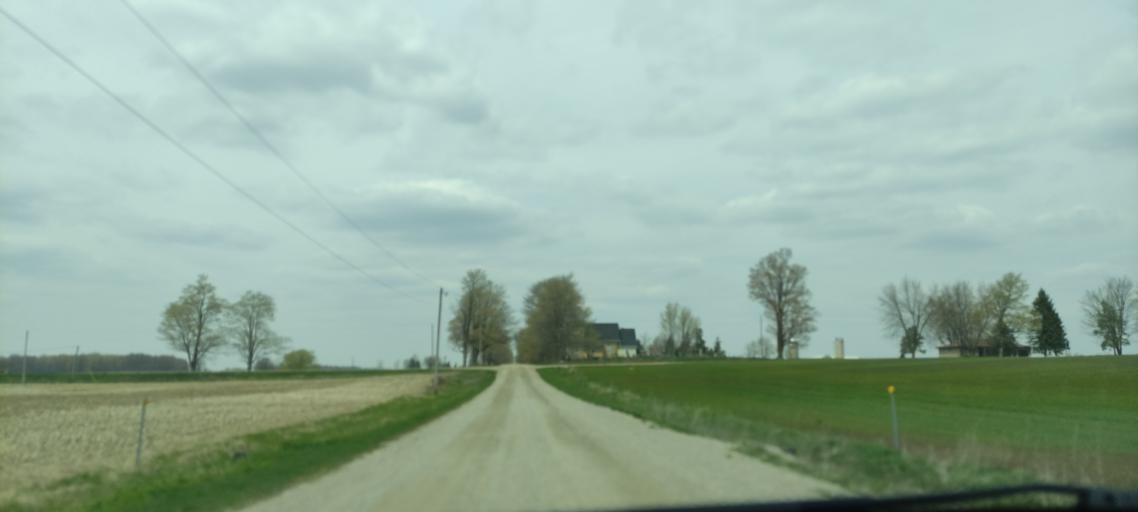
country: CA
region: Ontario
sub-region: Oxford County
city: Woodstock
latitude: 43.2850
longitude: -80.7477
